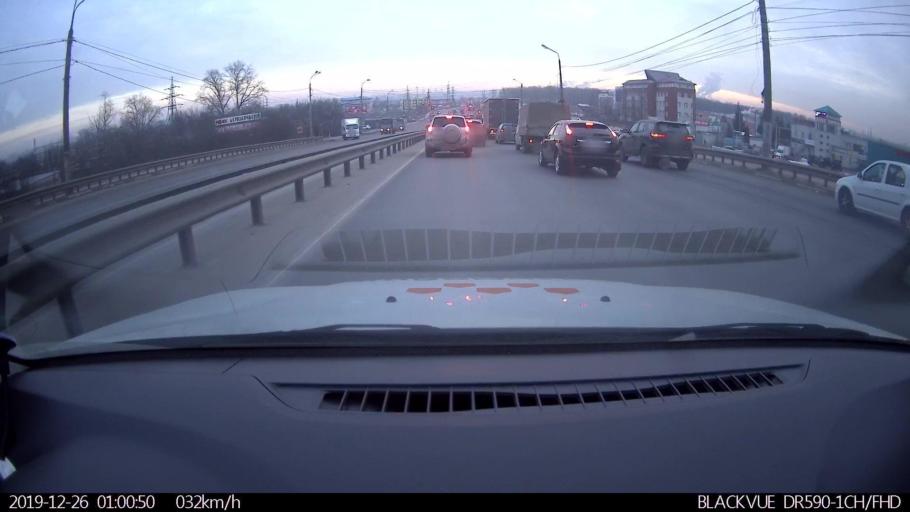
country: RU
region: Nizjnij Novgorod
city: Nizhniy Novgorod
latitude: 56.2941
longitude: 43.8821
